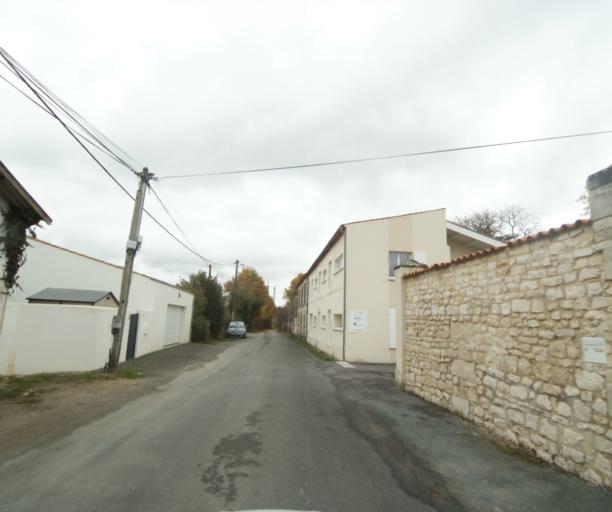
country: FR
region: Poitou-Charentes
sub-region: Departement de la Charente-Maritime
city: Saintes
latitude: 45.7636
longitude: -0.6262
